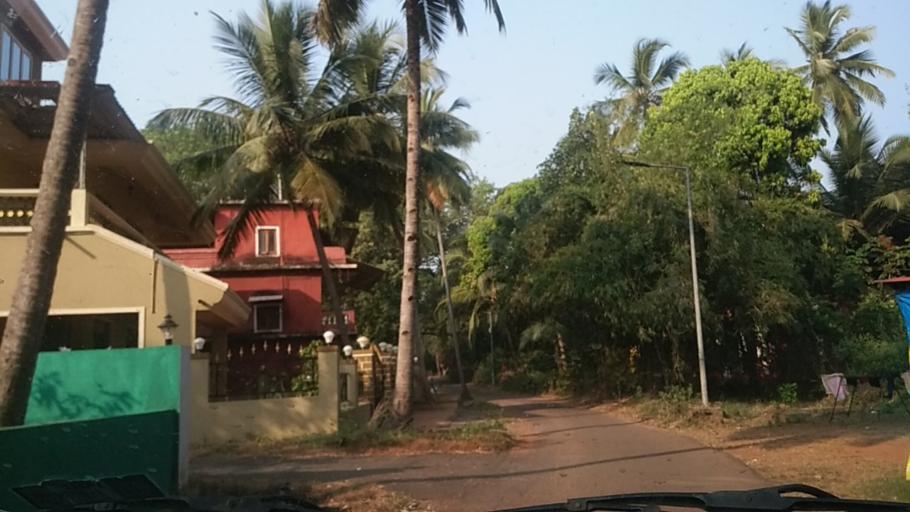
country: IN
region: Goa
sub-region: South Goa
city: Colva
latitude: 15.3151
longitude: 73.9341
